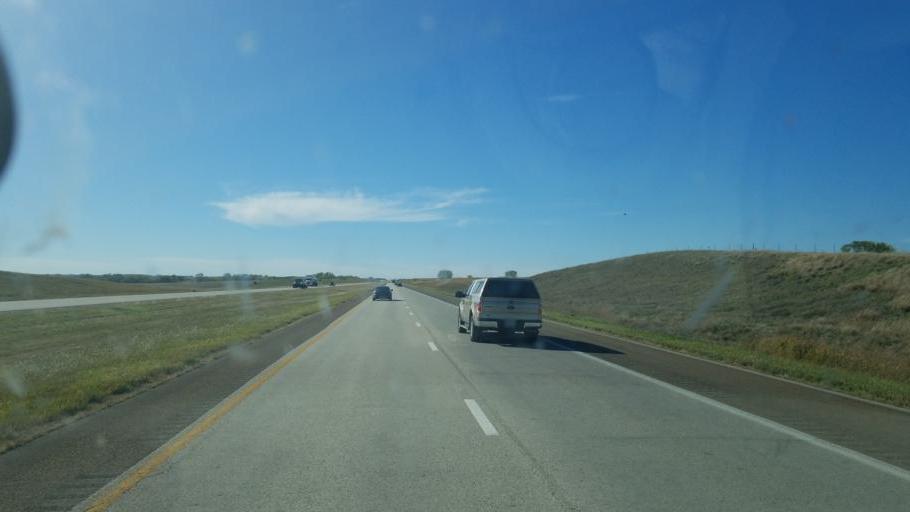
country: US
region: Kansas
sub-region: Saline County
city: Salina
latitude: 38.8778
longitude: -97.8273
